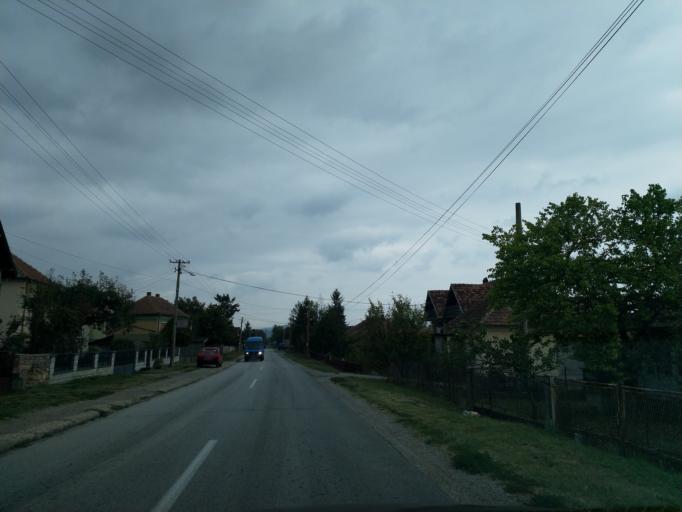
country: RS
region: Central Serbia
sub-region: Sumadijski Okrug
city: Batocina
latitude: 44.0785
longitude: 21.1813
